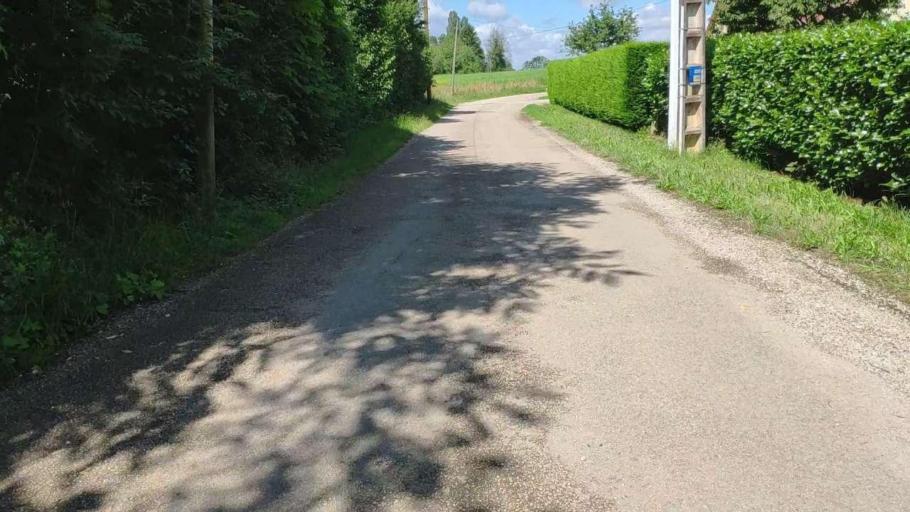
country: FR
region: Franche-Comte
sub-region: Departement du Jura
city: Bletterans
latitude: 46.8288
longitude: 5.5587
